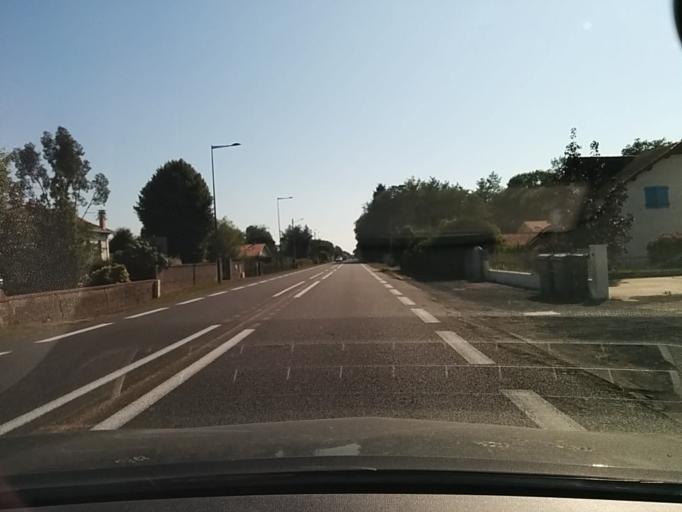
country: FR
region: Aquitaine
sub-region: Departement des Landes
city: Benesse-Maremne
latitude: 43.6325
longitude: -1.3623
